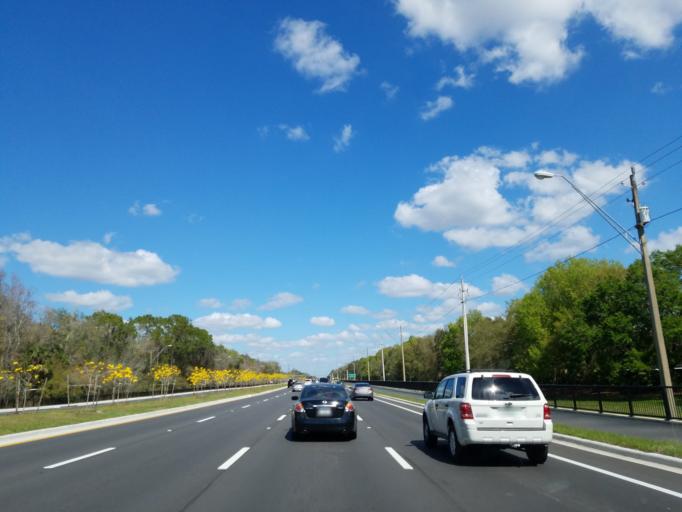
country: US
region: Florida
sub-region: Hillsborough County
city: University
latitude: 28.0937
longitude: -82.4024
